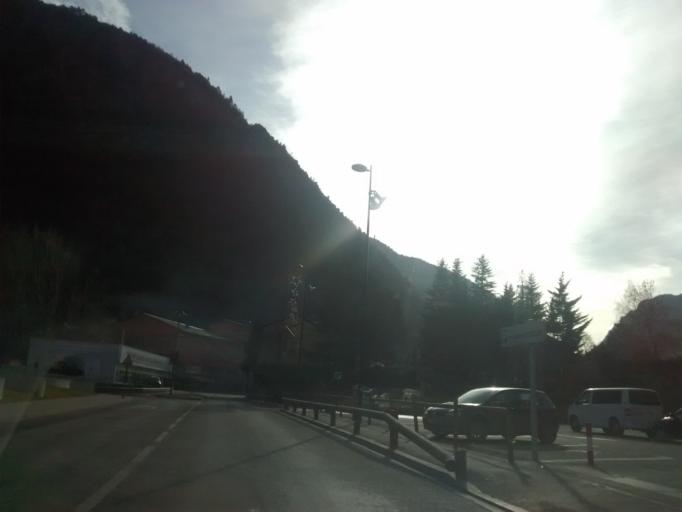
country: AD
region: Andorra la Vella
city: Andorra la Vella
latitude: 42.4950
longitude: 1.4981
